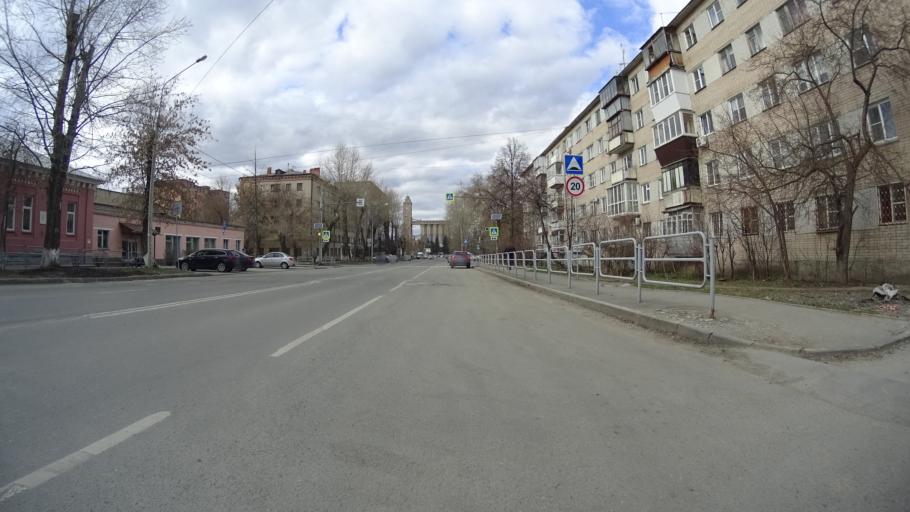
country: RU
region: Chelyabinsk
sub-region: Gorod Chelyabinsk
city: Chelyabinsk
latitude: 55.1654
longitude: 61.3860
